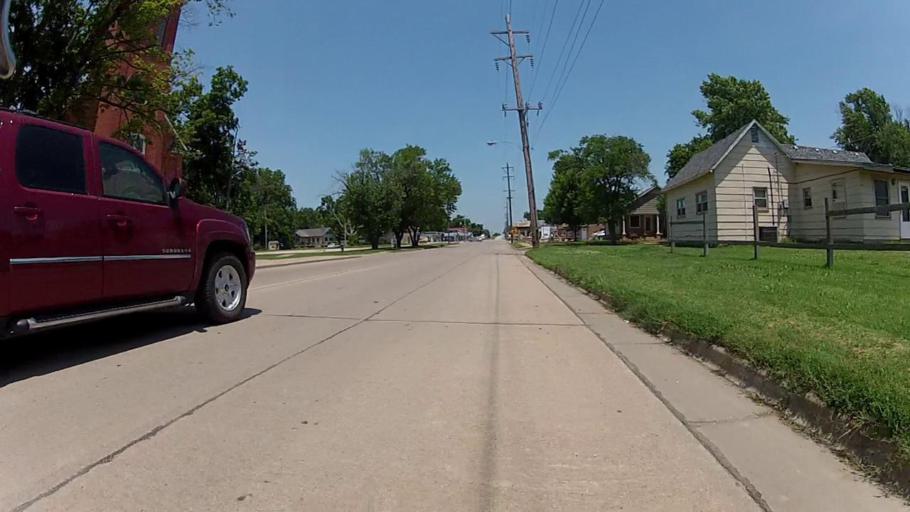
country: US
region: Kansas
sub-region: Montgomery County
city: Cherryvale
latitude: 37.2675
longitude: -95.5555
